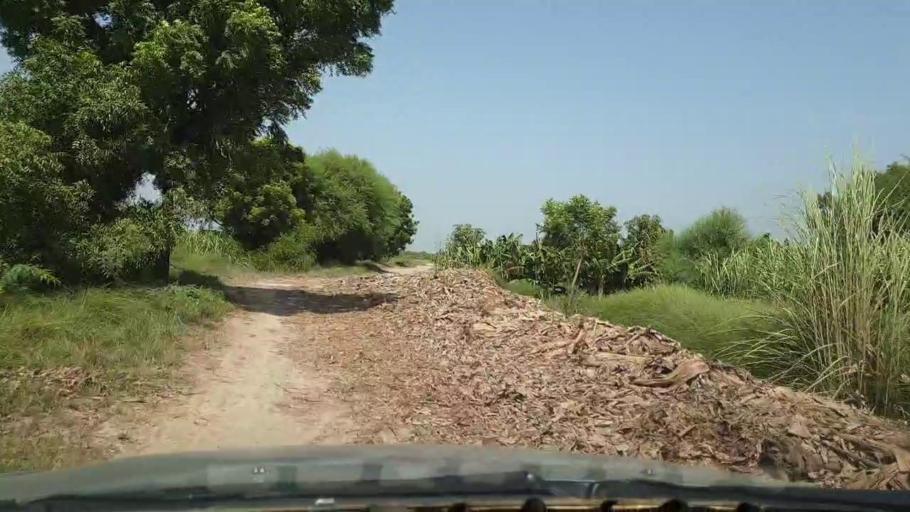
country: PK
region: Sindh
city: Tando Muhammad Khan
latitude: 25.1826
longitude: 68.6326
